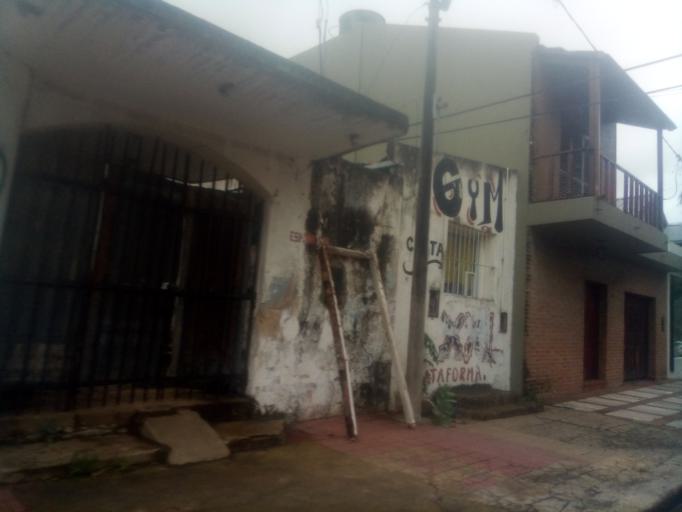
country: AR
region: Corrientes
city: Corrientes
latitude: -27.4641
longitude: -58.8288
